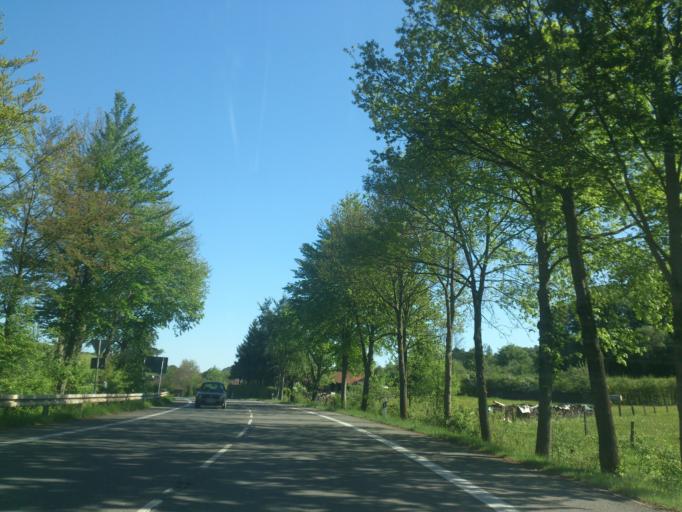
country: DE
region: North Rhine-Westphalia
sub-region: Regierungsbezirk Detmold
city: Willebadessen
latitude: 51.6689
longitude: 9.0030
